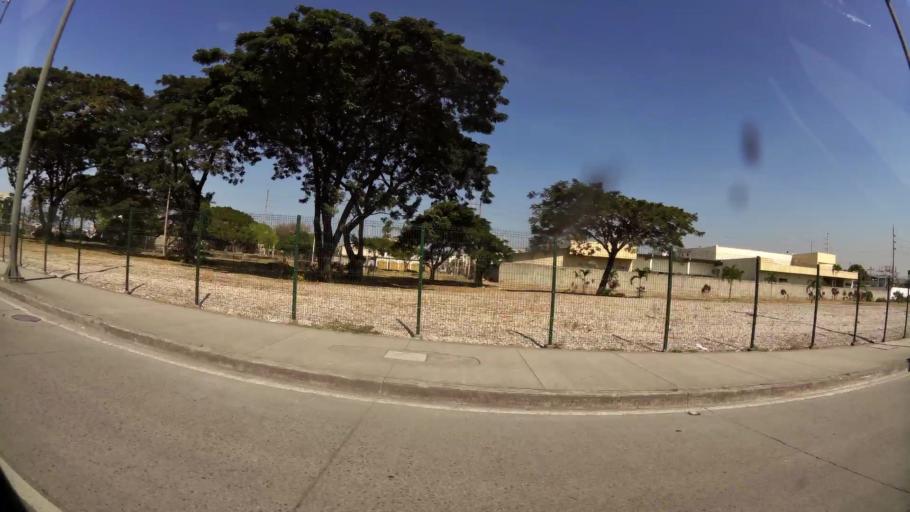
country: EC
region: Guayas
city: Eloy Alfaro
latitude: -2.1401
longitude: -79.8830
